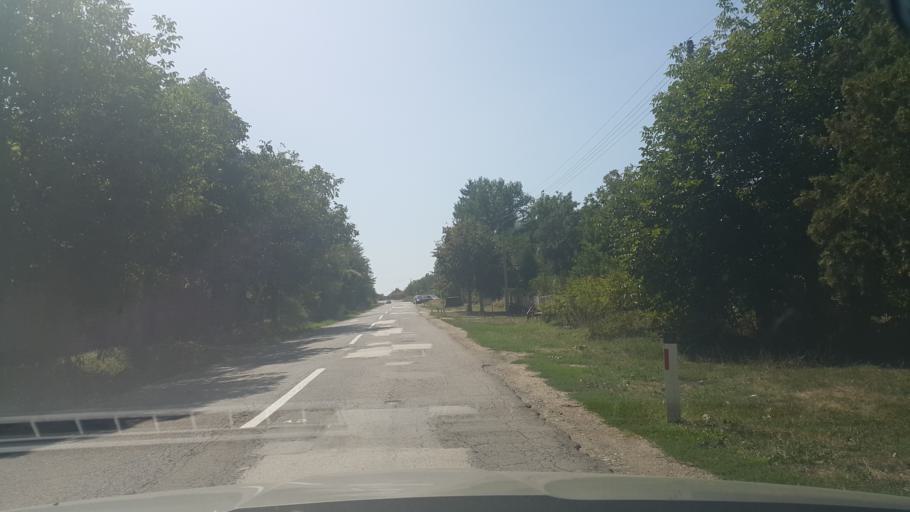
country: RS
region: Central Serbia
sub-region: Zajecarski Okrug
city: Knjazevac
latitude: 43.7301
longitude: 22.3099
